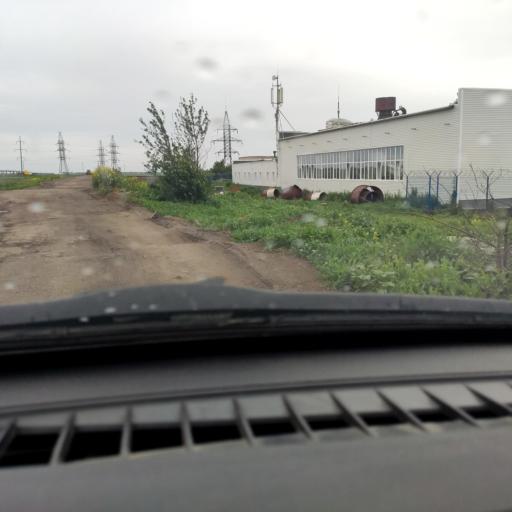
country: RU
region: Samara
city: Tol'yatti
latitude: 53.5919
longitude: 49.4391
